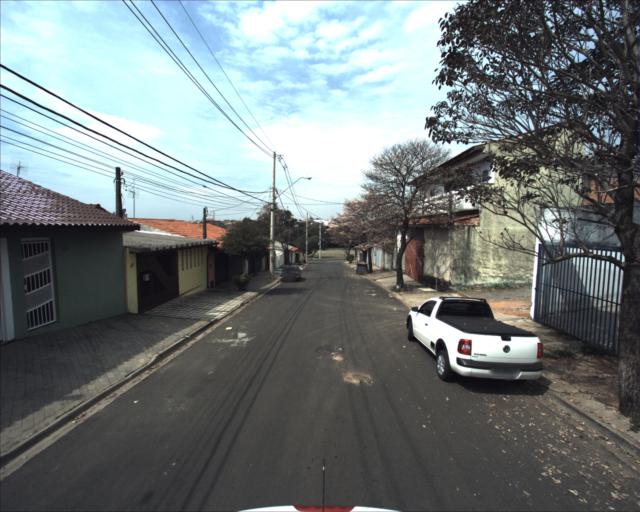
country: BR
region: Sao Paulo
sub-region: Sorocaba
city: Sorocaba
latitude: -23.5020
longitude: -47.5235
